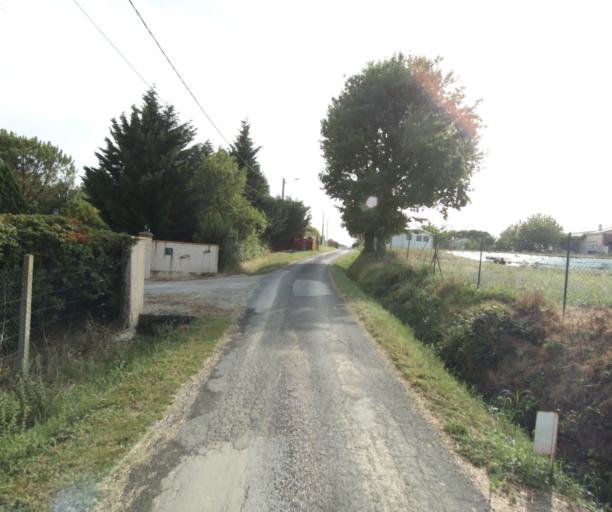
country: FR
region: Midi-Pyrenees
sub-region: Departement du Tarn
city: Soual
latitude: 43.5424
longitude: 2.0635
